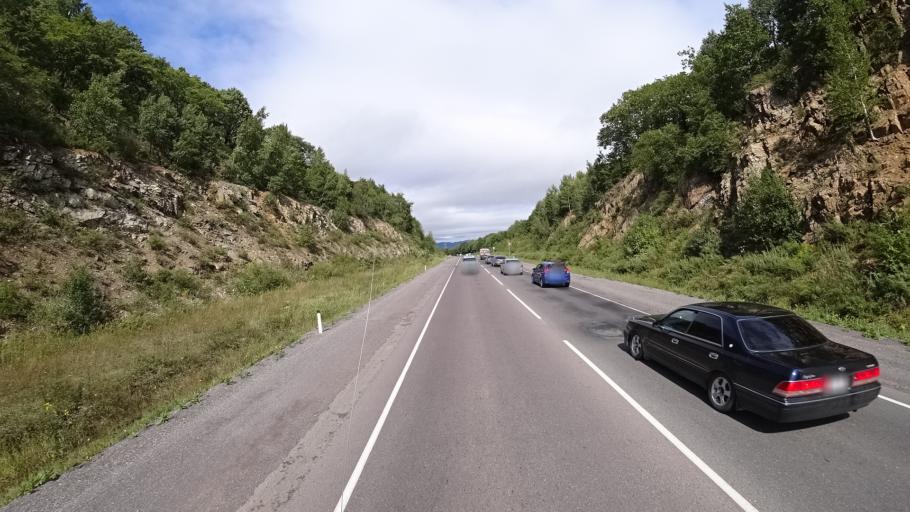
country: RU
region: Primorskiy
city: Lyalichi
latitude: 44.1282
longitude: 132.4256
